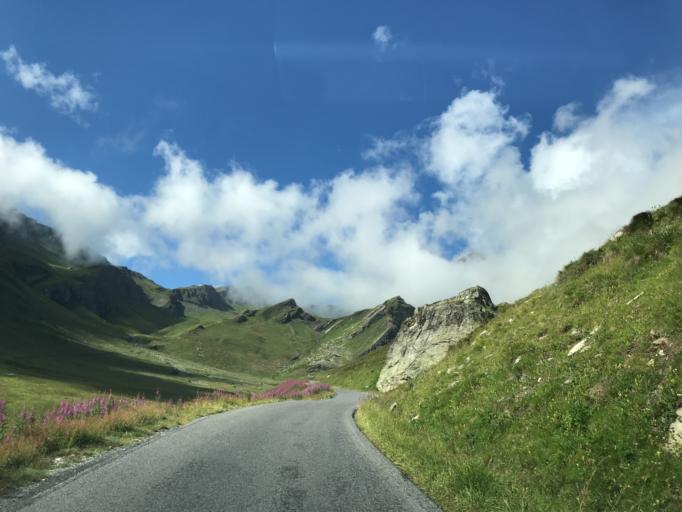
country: IT
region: Piedmont
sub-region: Provincia di Cuneo
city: Pontechianale
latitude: 44.6647
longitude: 6.9868
